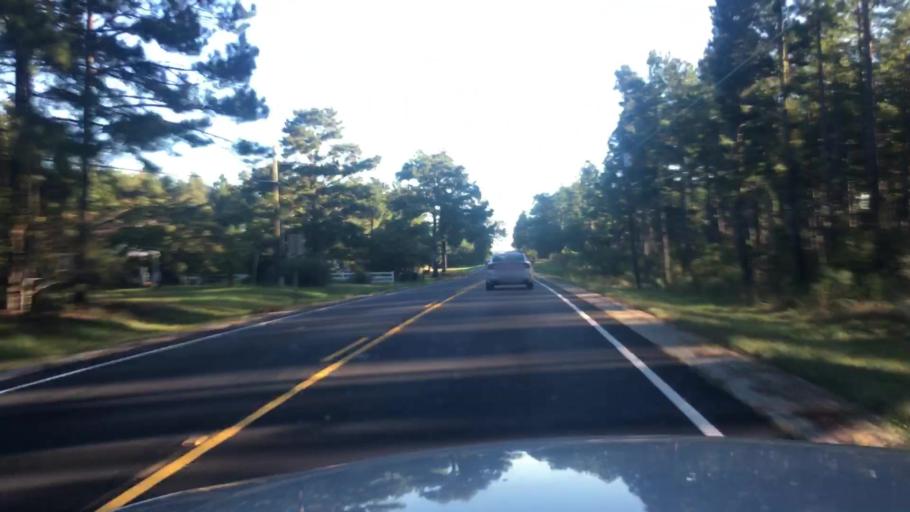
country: US
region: North Carolina
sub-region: Harnett County
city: Walkertown
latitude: 35.3329
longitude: -78.8616
